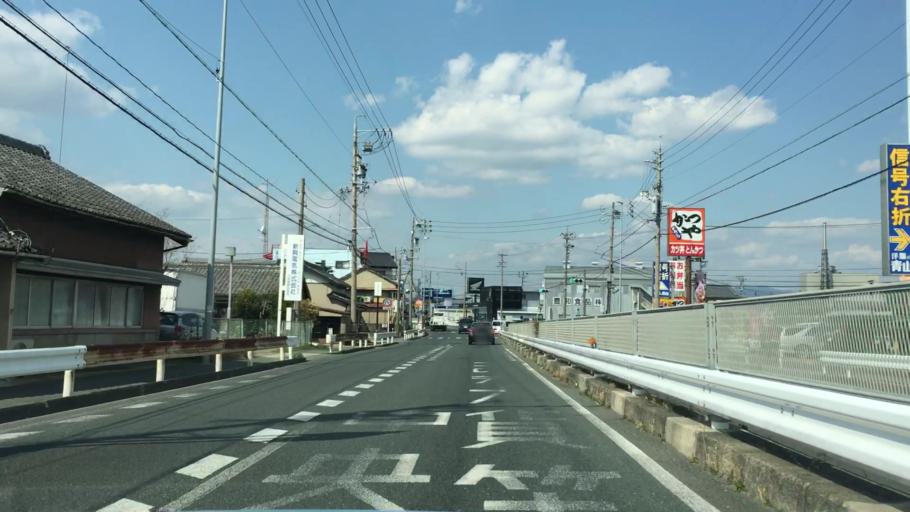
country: JP
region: Aichi
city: Toyohashi
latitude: 34.7507
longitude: 137.4129
